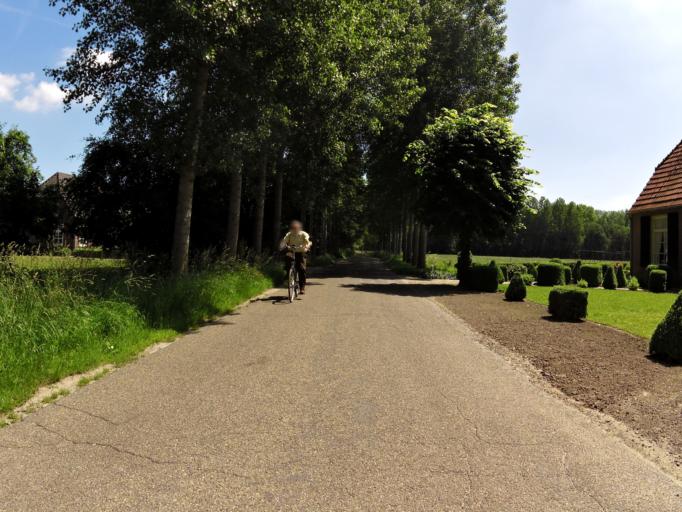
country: NL
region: North Brabant
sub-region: Gemeente Boxtel
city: Boxtel
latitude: 51.5904
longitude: 5.3676
